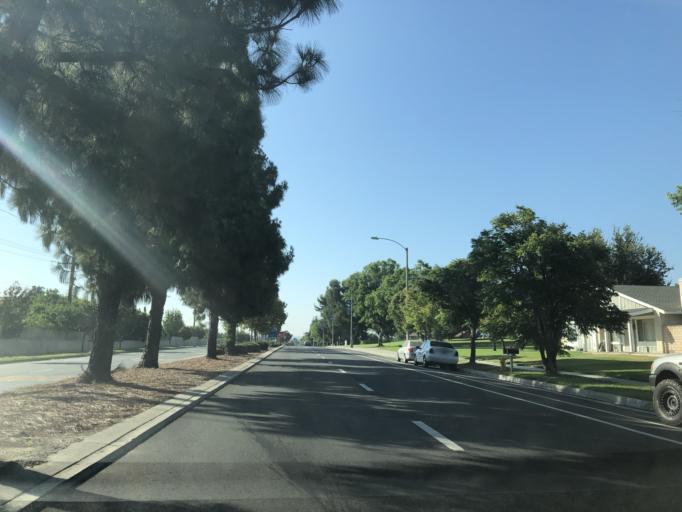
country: US
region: California
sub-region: Riverside County
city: Corona
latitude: 33.9018
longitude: -117.5769
